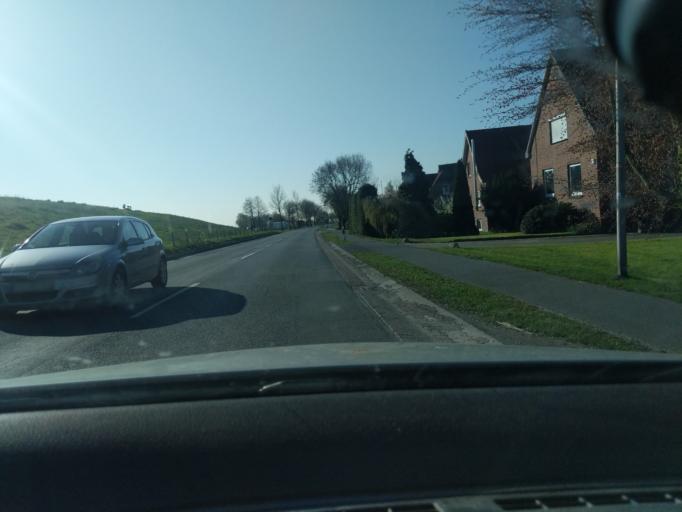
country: DE
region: Lower Saxony
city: Mittelnkirchen
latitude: 53.5634
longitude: 9.6524
